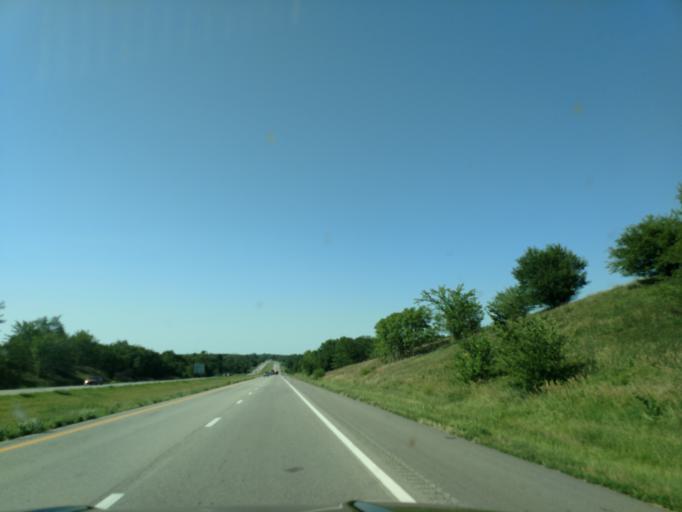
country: US
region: Missouri
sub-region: Andrew County
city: Country Club Village
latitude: 39.8320
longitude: -94.8052
